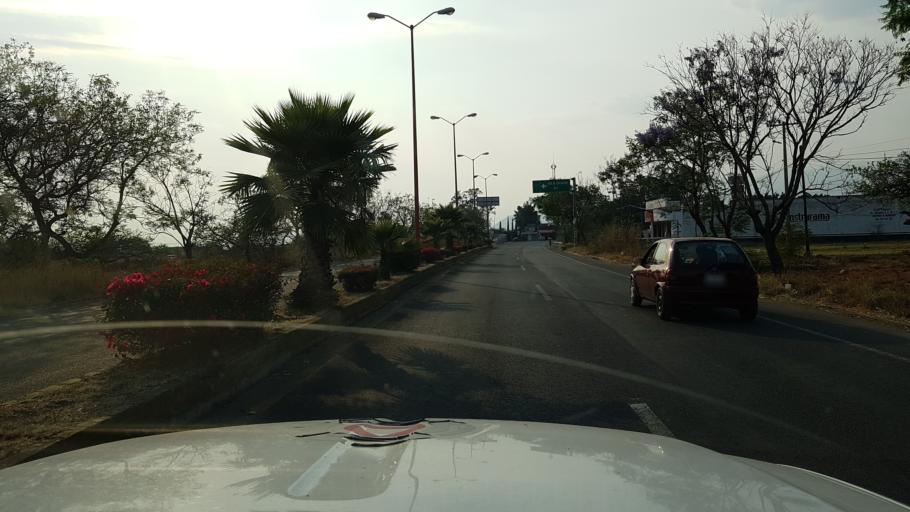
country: MX
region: Morelos
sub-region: Atlatlahucan
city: Colonia San Francisco
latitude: 18.8964
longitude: -98.9061
